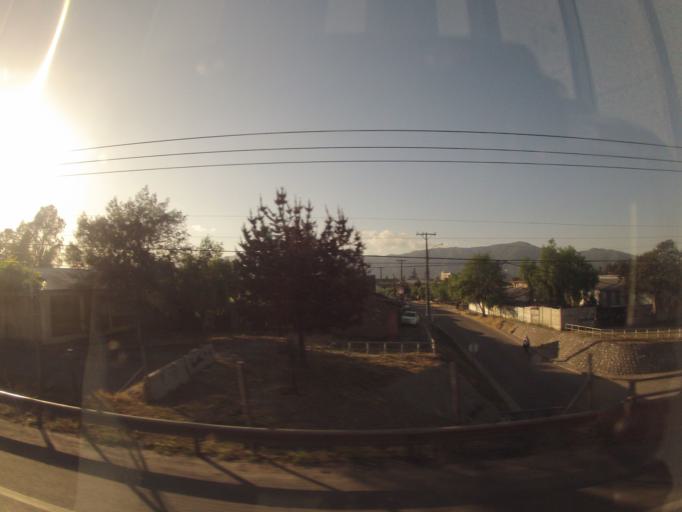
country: CL
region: O'Higgins
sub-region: Provincia de Colchagua
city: Chimbarongo
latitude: -34.5979
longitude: -70.9760
